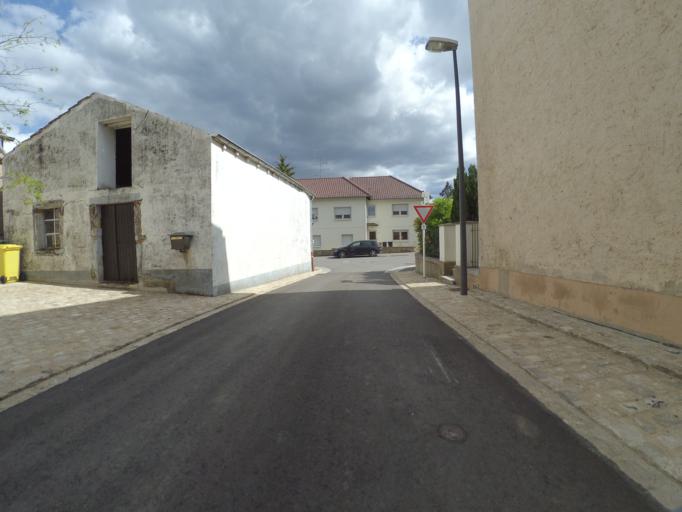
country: LU
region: Grevenmacher
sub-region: Canton de Remich
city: Mondorf-les-Bains
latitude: 49.5211
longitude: 6.2974
